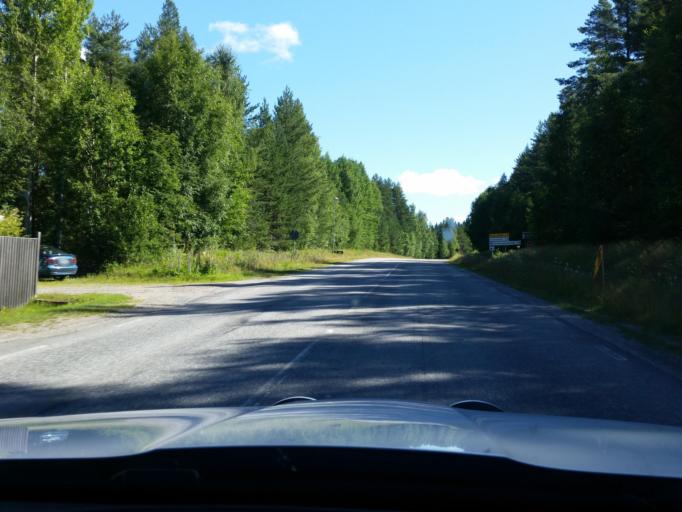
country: SE
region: Norrbotten
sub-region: Pitea Kommun
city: Roknas
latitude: 65.3183
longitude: 21.2566
